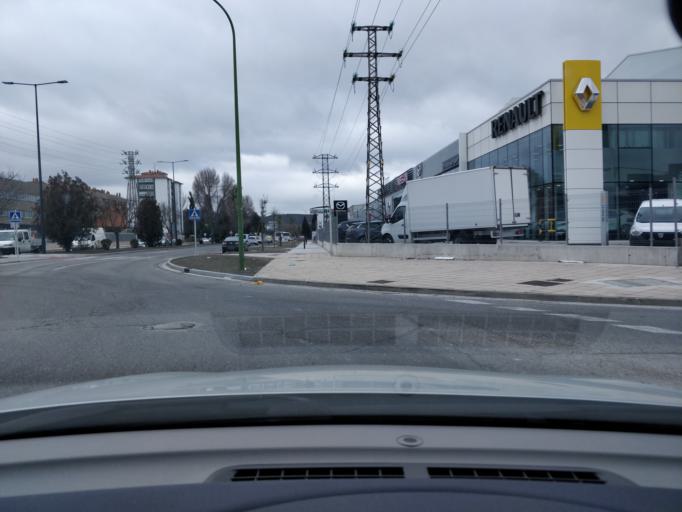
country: ES
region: Castille and Leon
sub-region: Provincia de Burgos
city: Burgos
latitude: 42.3606
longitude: -3.6521
